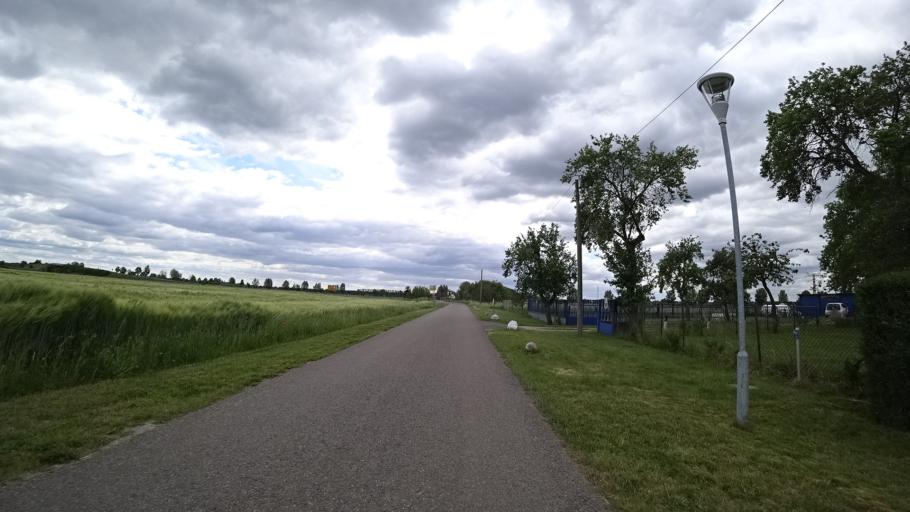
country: DE
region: Brandenburg
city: Trebbin
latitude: 52.1873
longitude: 13.2451
